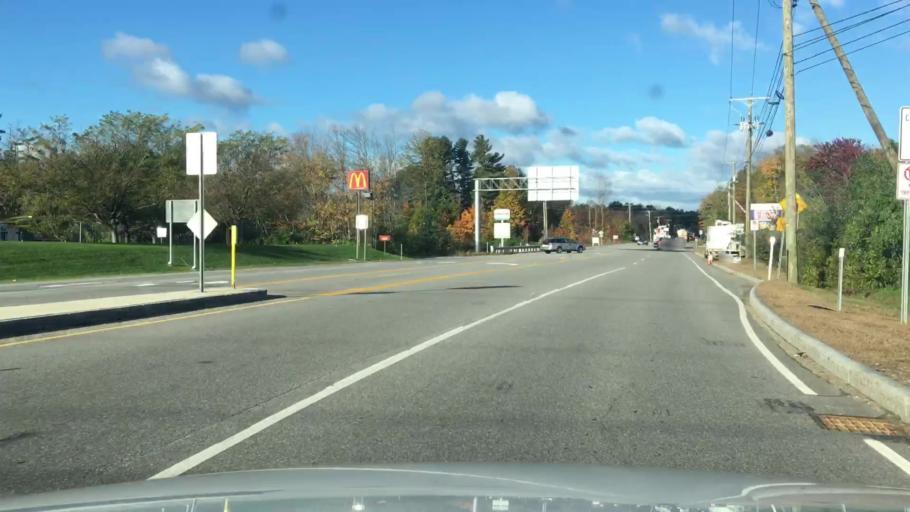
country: US
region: New Hampshire
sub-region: Strafford County
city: Lee
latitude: 43.1493
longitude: -71.0072
